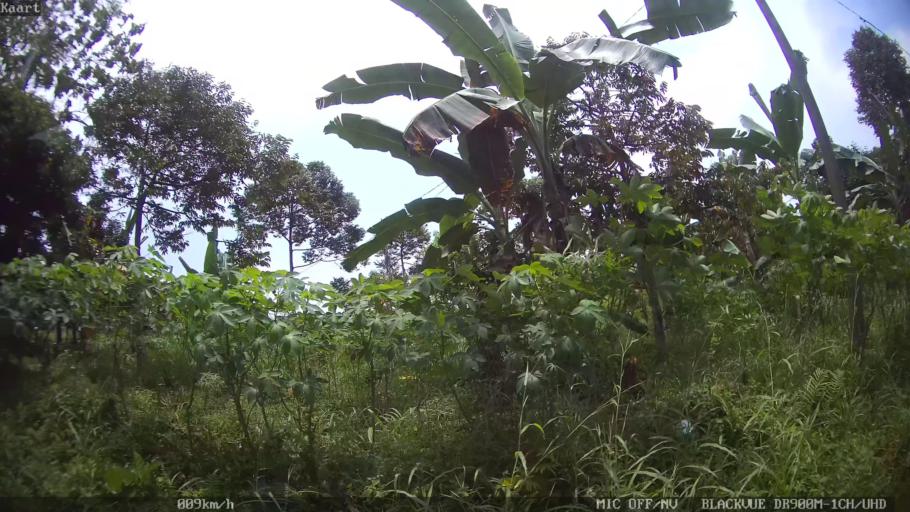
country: ID
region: Lampung
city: Bandarlampung
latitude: -5.4115
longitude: 105.2060
